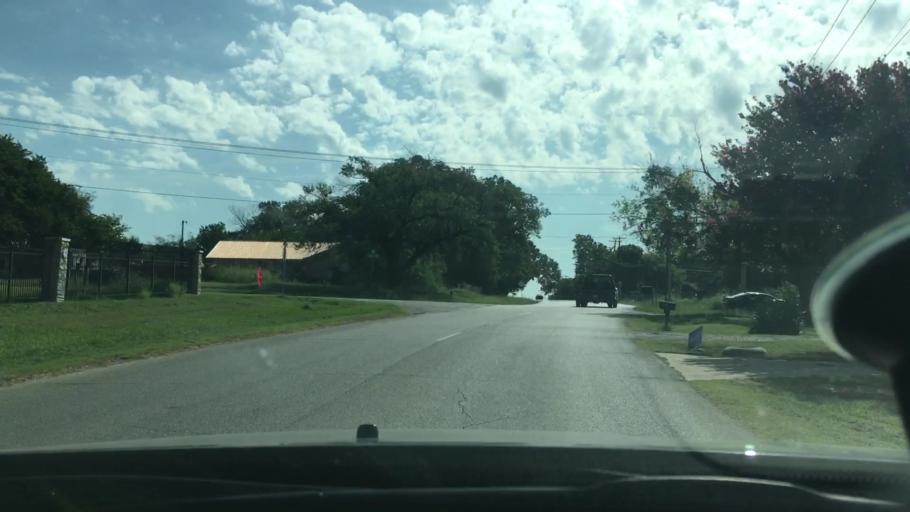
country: US
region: Oklahoma
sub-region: Carter County
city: Ardmore
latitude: 34.1585
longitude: -97.1187
